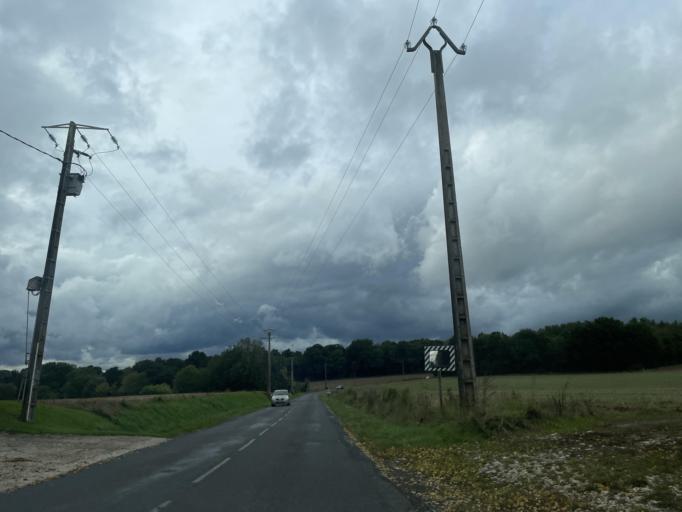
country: FR
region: Ile-de-France
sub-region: Departement de Seine-et-Marne
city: Saint-Jean-les-Deux-Jumeaux
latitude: 48.9329
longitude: 2.9917
